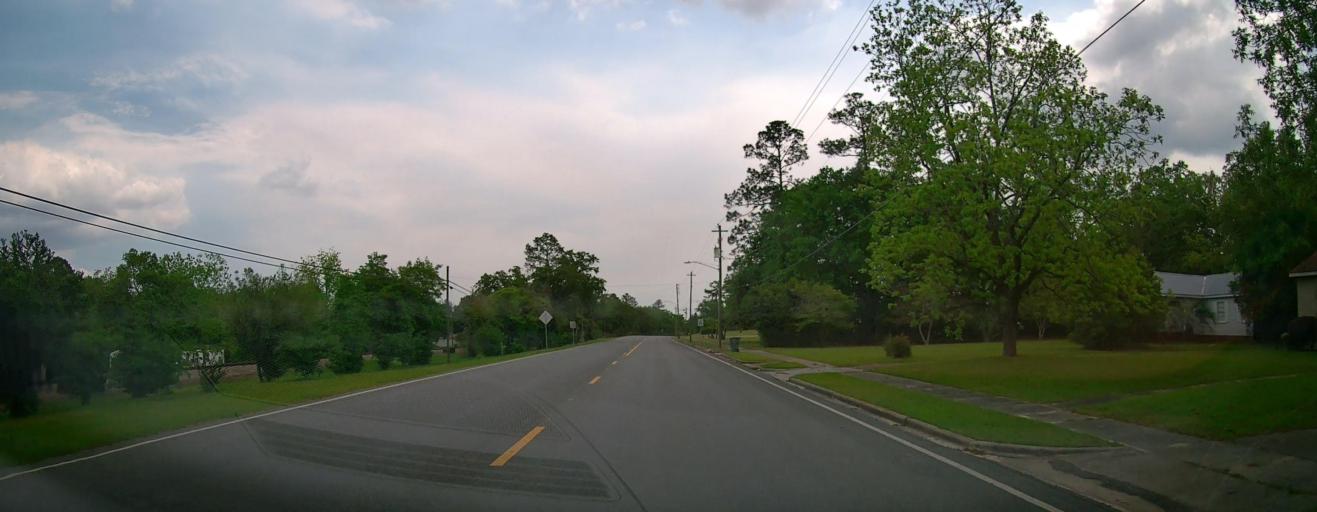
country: US
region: Georgia
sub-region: Treutlen County
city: Soperton
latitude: 32.3696
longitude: -82.5847
